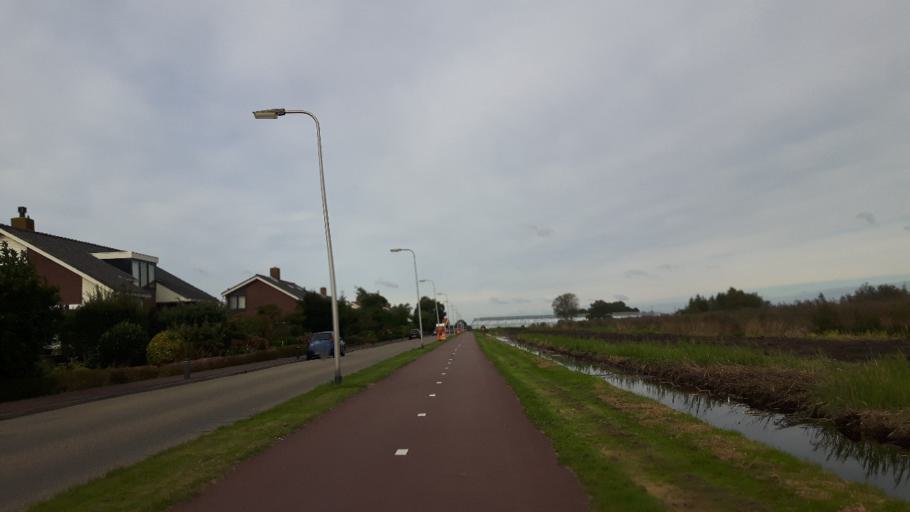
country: NL
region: Utrecht
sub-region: Gemeente De Ronde Venen
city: Mijdrecht
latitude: 52.1666
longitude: 4.8296
